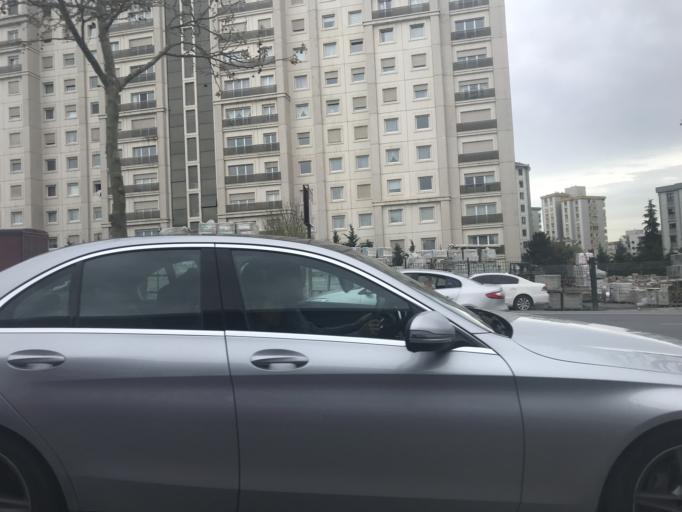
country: TR
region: Istanbul
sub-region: Atasehir
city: Atasehir
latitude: 40.9865
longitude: 29.1388
